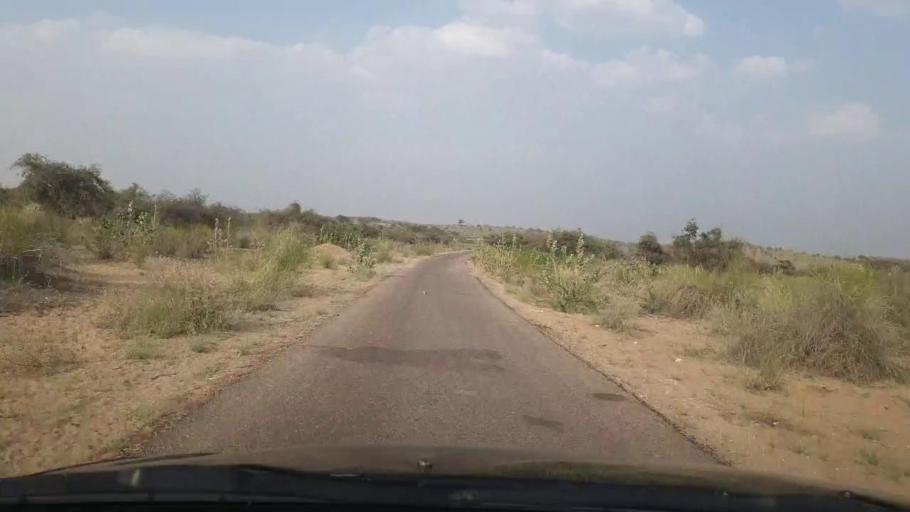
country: PK
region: Sindh
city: Islamkot
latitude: 25.0639
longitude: 70.5635
